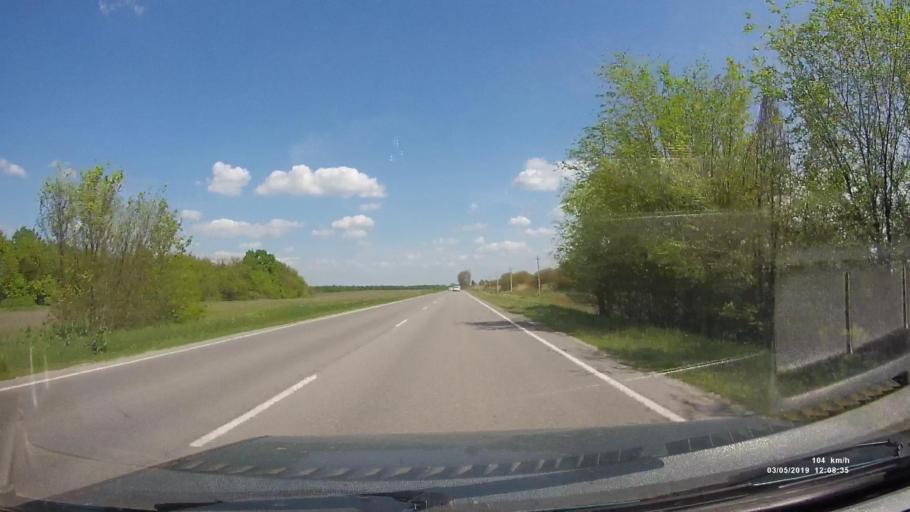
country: RU
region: Rostov
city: Bagayevskaya
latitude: 47.2884
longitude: 40.4990
